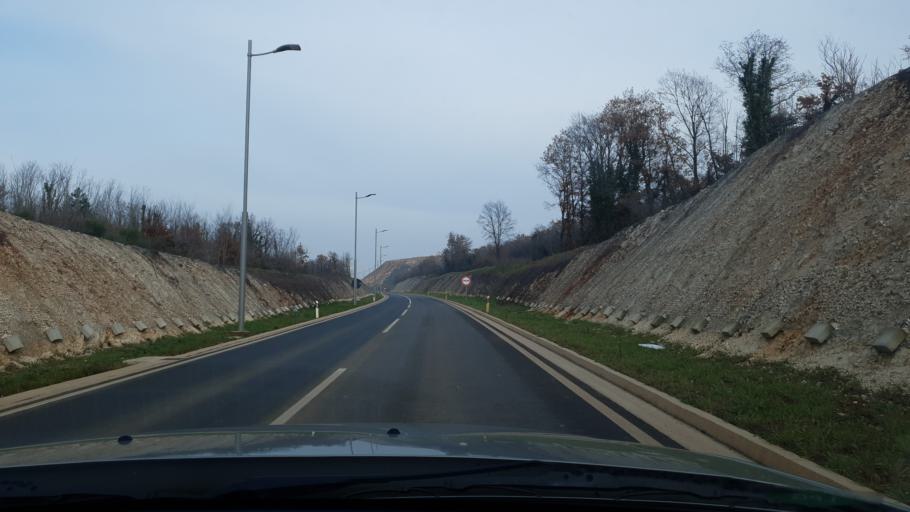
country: HR
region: Istarska
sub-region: Grad Porec
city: Porec
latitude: 45.2044
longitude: 13.6149
